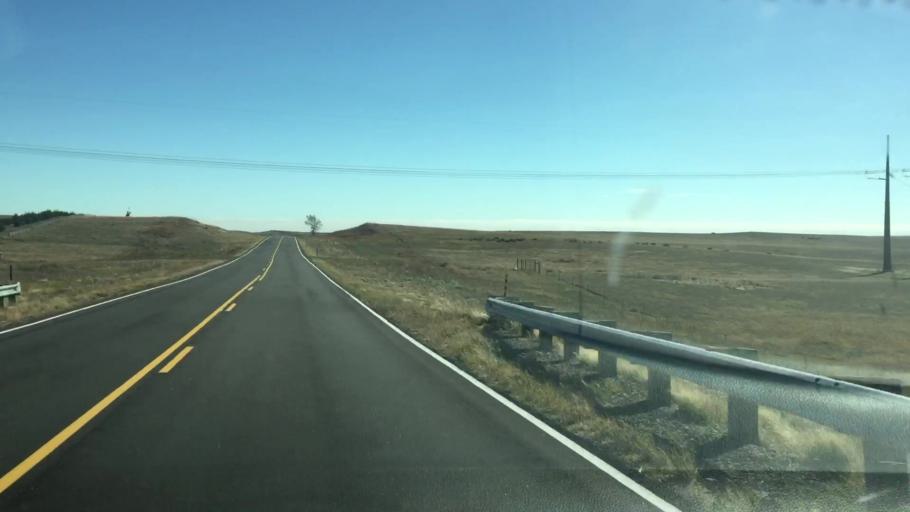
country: US
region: Colorado
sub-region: Lincoln County
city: Limon
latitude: 39.2954
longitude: -103.8734
